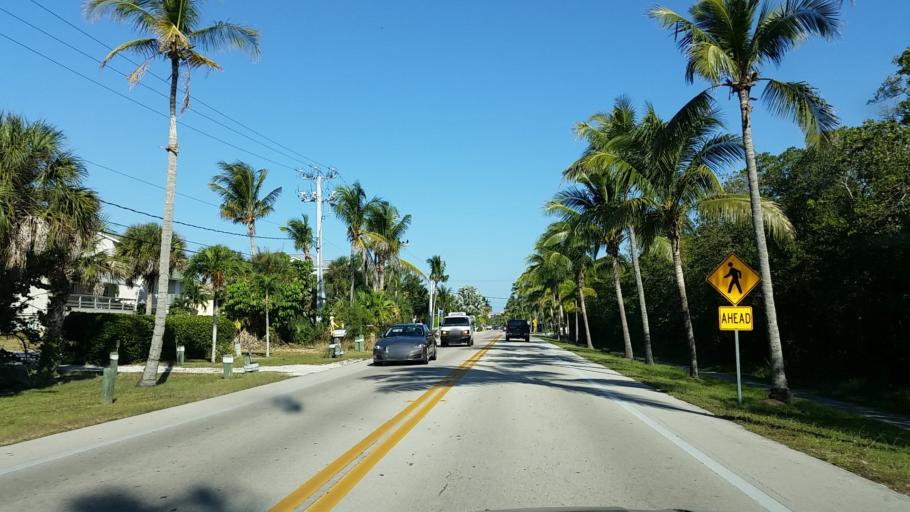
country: US
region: Florida
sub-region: Lee County
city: Bonita Springs
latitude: 26.3434
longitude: -81.8505
